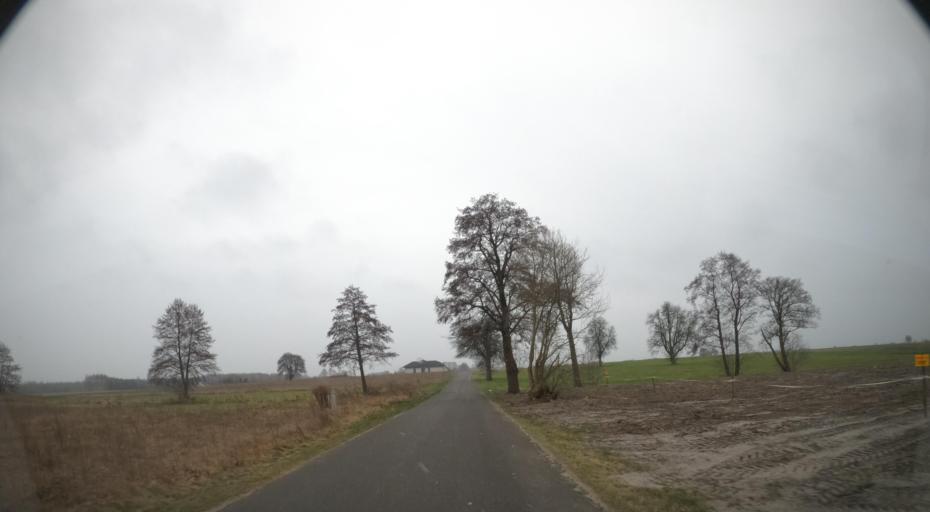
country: PL
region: Masovian Voivodeship
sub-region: Powiat radomski
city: Jedlnia-Letnisko
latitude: 51.4122
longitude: 21.2929
